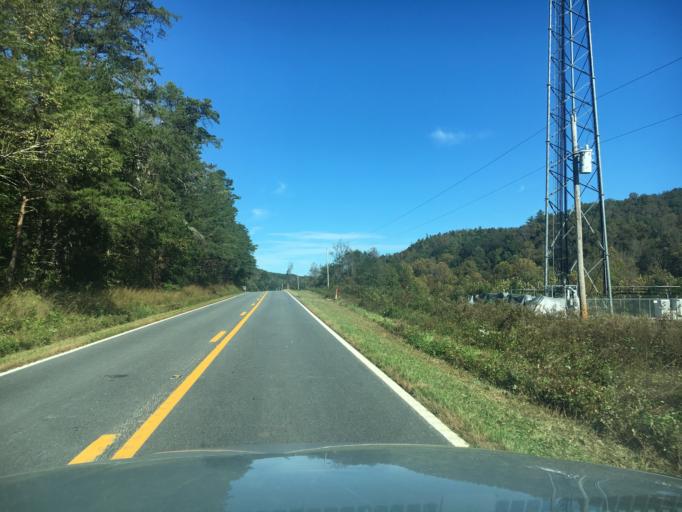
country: US
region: North Carolina
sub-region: Rutherford County
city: Spindale
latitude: 35.5354
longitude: -81.8563
